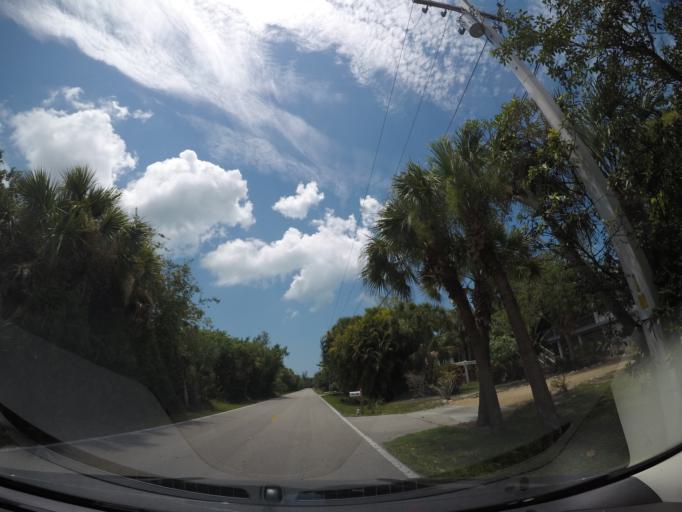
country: US
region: Florida
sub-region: Lee County
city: Saint James City
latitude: 26.4338
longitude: -82.1080
